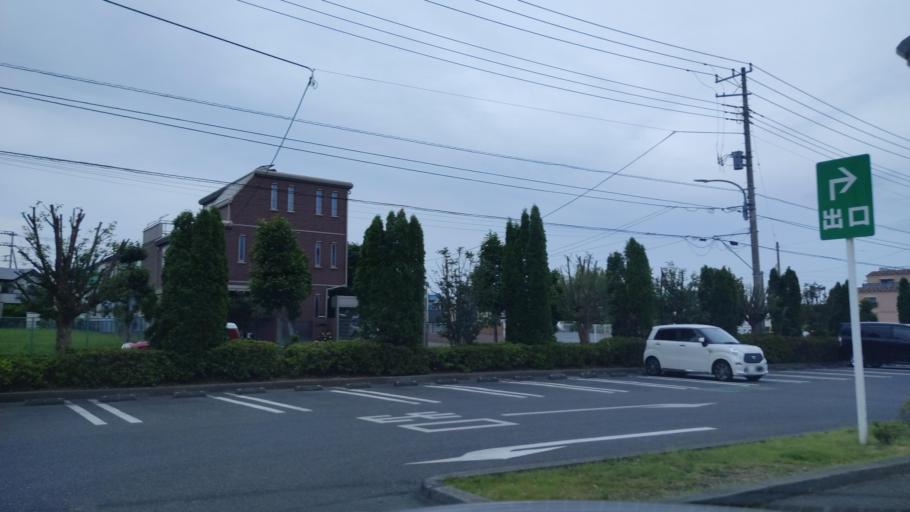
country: JP
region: Chiba
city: Kashiwa
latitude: 35.8832
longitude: 139.9700
